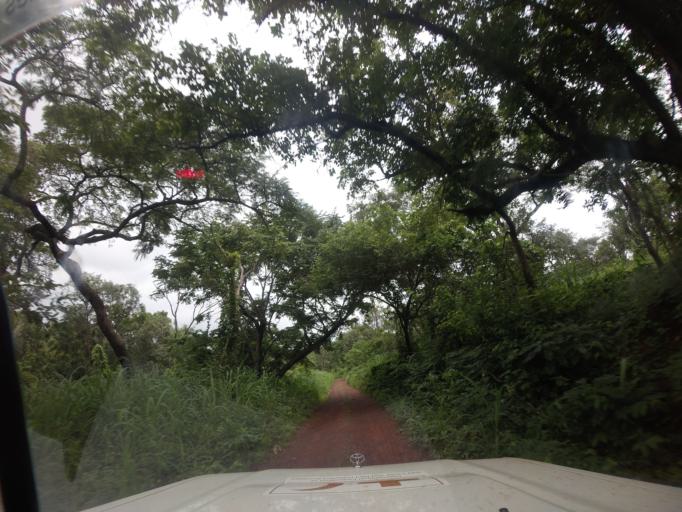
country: SL
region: Northern Province
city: Kamakwie
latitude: 9.6834
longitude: -12.2493
